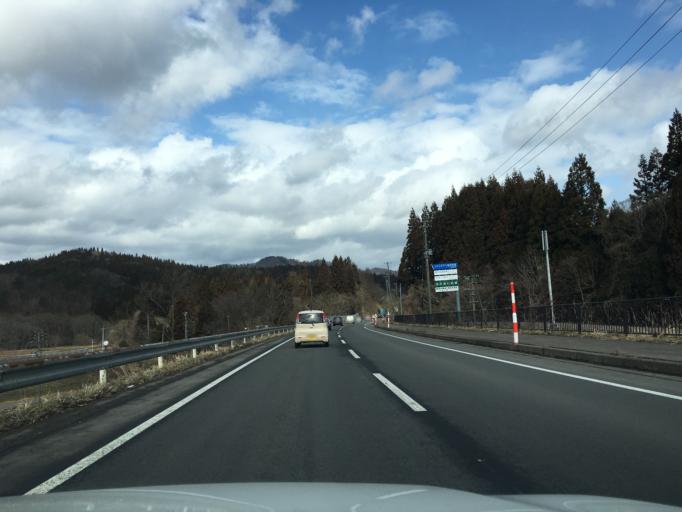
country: JP
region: Akita
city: Takanosu
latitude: 40.0262
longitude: 140.2739
